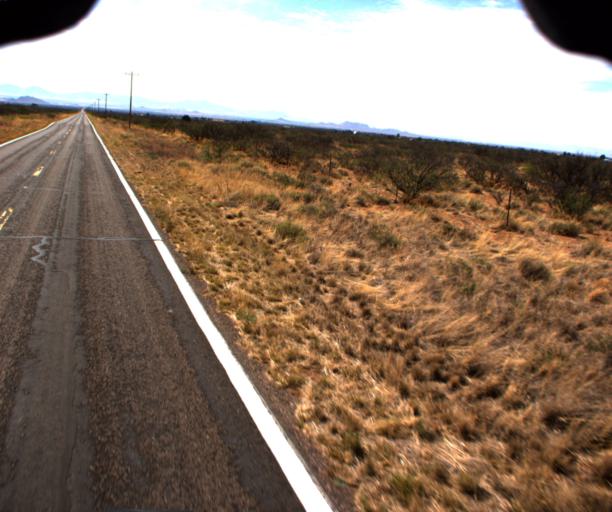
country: US
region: Arizona
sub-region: Cochise County
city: Willcox
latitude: 31.8760
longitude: -109.5072
